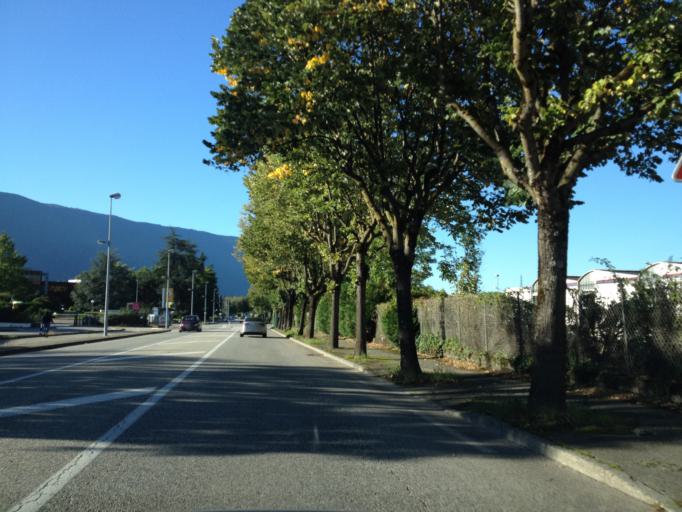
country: FR
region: Rhone-Alpes
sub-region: Departement de la Savoie
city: La Motte-Servolex
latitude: 45.5857
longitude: 5.8846
